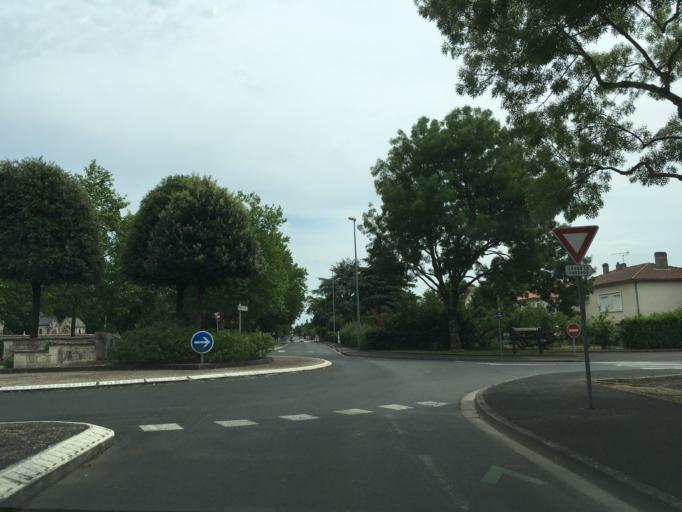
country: FR
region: Poitou-Charentes
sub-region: Departement des Deux-Sevres
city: Bessines
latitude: 46.3232
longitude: -0.5124
